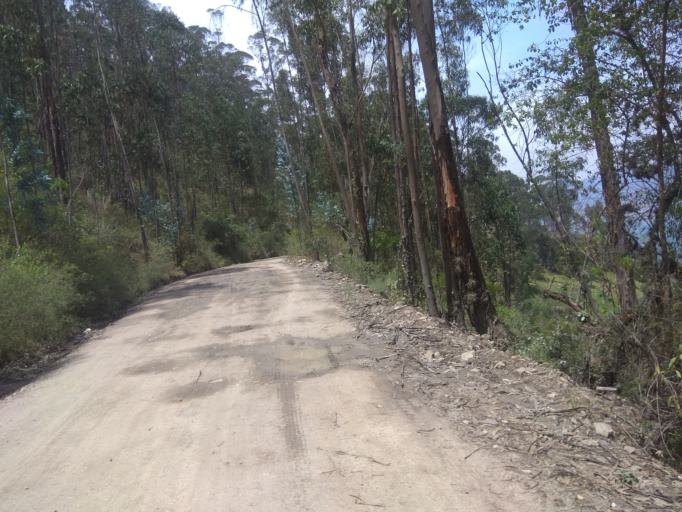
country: CO
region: Boyaca
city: Socha Viejo
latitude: 5.9805
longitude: -72.7340
